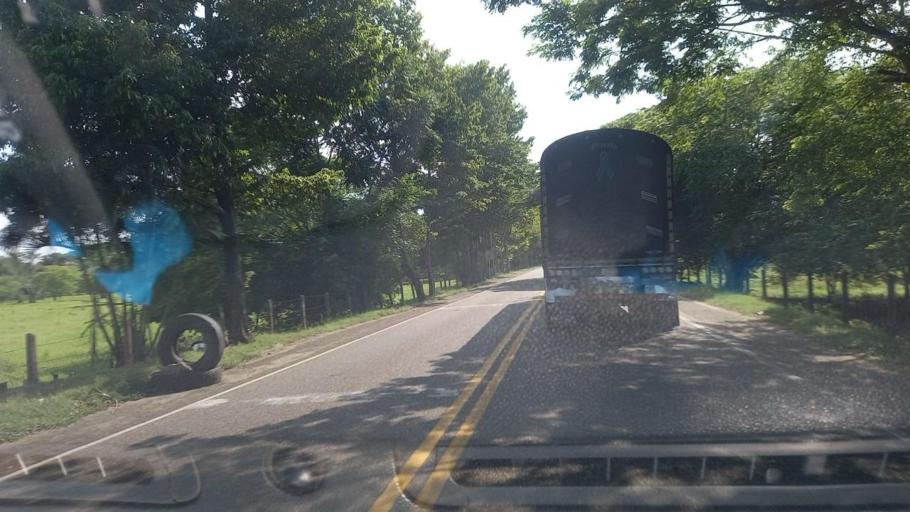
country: CO
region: Antioquia
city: Puerto Berrio
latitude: 6.3273
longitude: -74.4370
